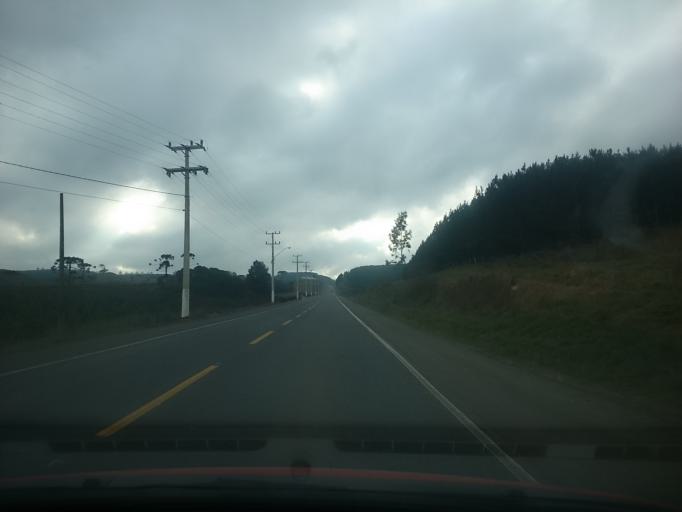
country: BR
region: Santa Catarina
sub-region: Lages
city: Lages
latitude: -27.8441
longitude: -50.3745
